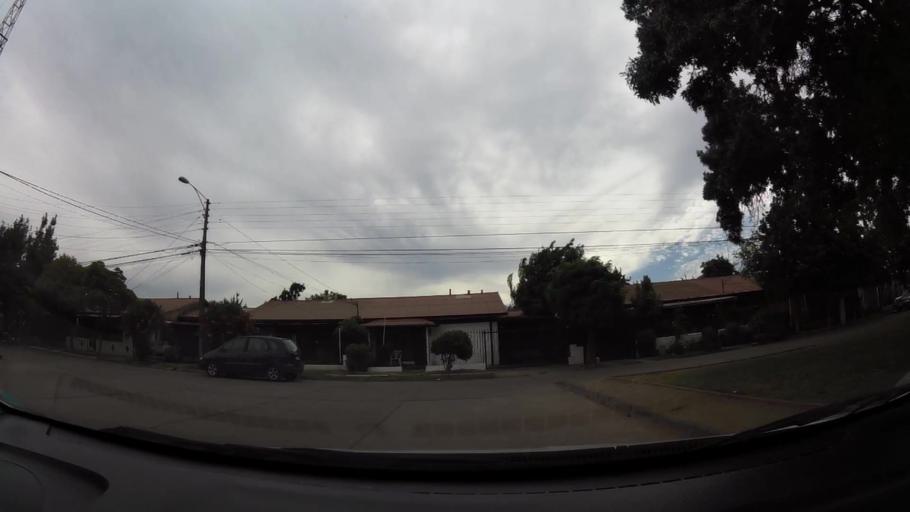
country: CL
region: O'Higgins
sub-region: Provincia de Cachapoal
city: Rancagua
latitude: -34.1541
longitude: -70.7392
